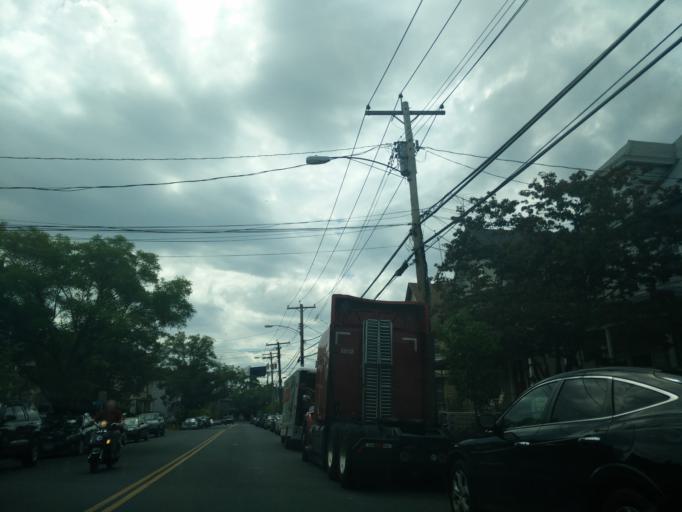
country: US
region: Connecticut
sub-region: Fairfield County
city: Bridgeport
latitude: 41.1710
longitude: -73.2012
